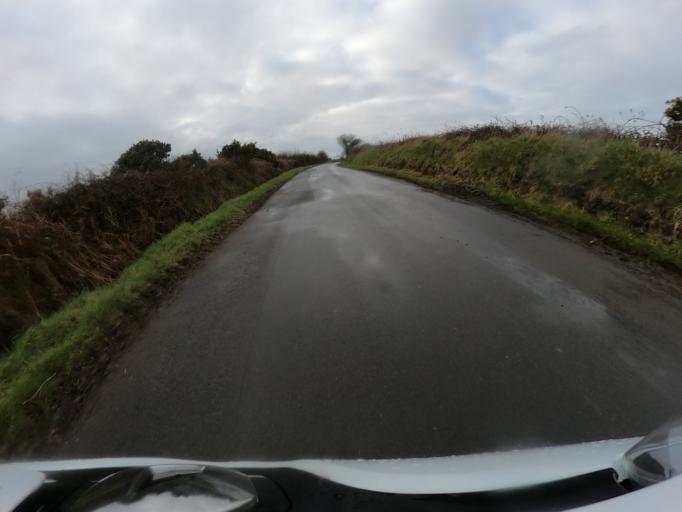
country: IM
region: Ramsey
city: Ramsey
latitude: 54.3642
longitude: -4.4982
